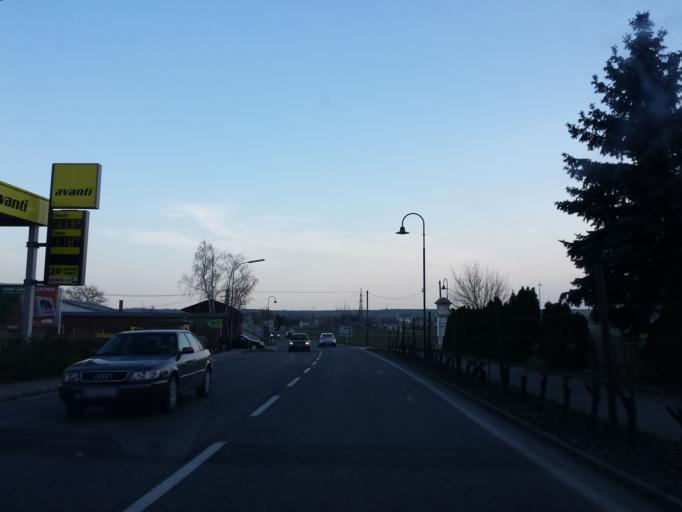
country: AT
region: Lower Austria
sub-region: Politischer Bezirk Mistelbach
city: Poysdorf
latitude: 48.6595
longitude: 16.6291
